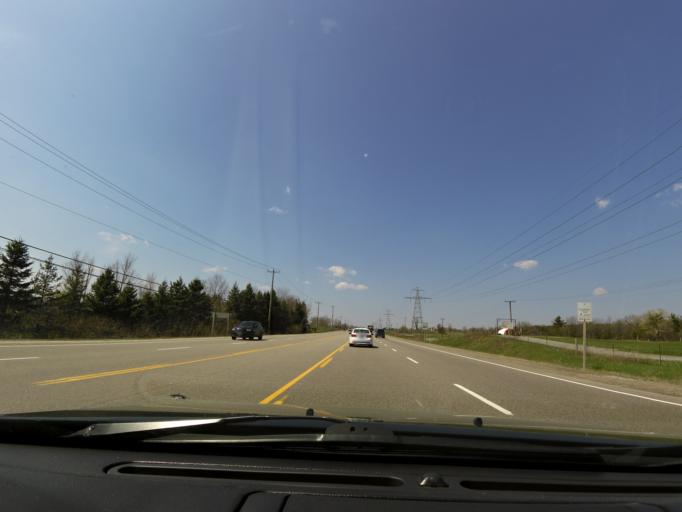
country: CA
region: Ontario
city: Ancaster
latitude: 43.3892
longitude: -80.0221
